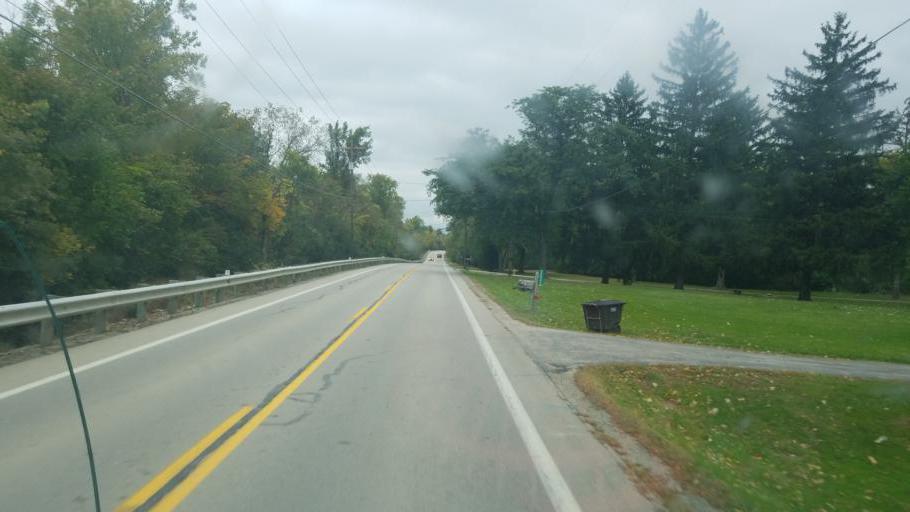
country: US
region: Ohio
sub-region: Wood County
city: Haskins
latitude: 41.4783
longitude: -83.7097
